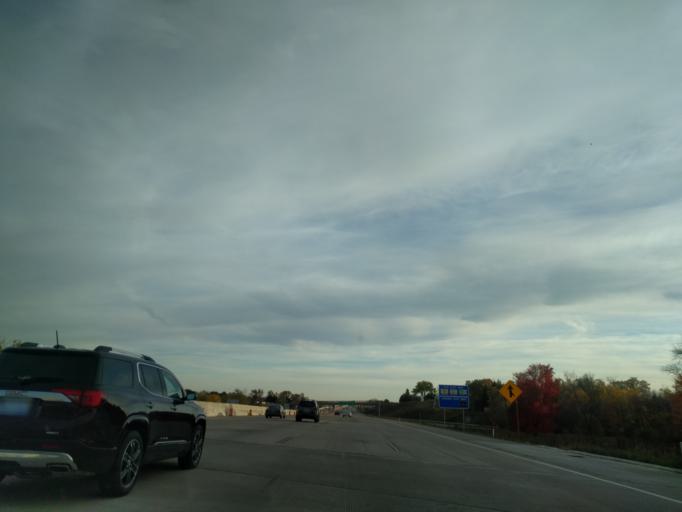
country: US
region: Wisconsin
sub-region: Brown County
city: Ashwaubenon
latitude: 44.4836
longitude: -88.0806
